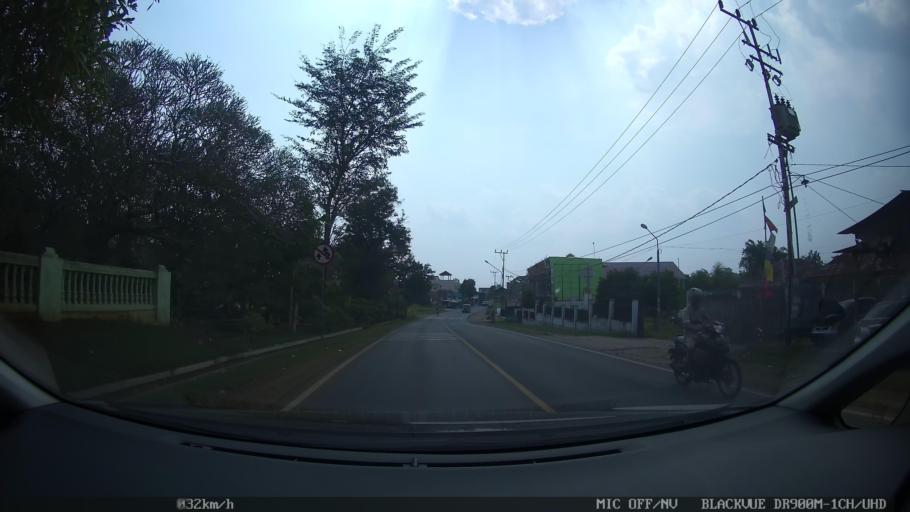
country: ID
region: Lampung
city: Gadingrejo
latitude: -5.3750
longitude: 105.0644
